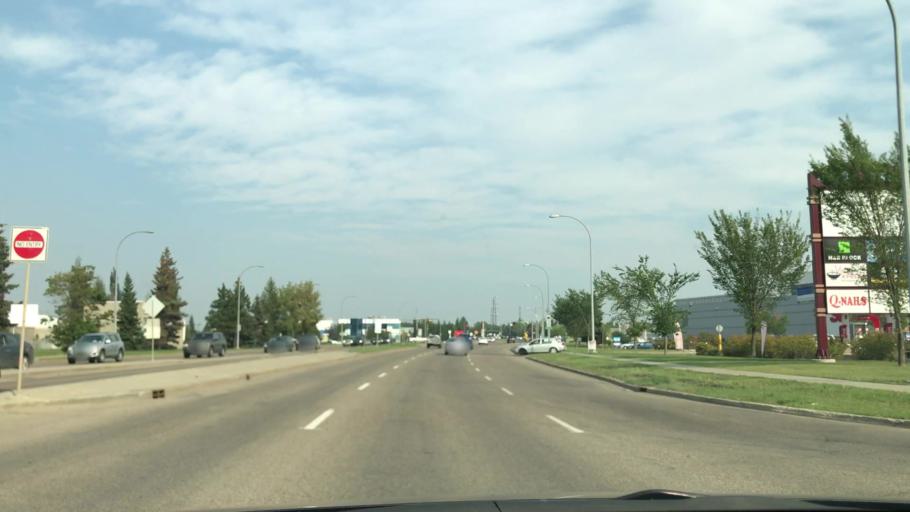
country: CA
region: Alberta
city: Edmonton
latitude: 53.4537
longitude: -113.4830
